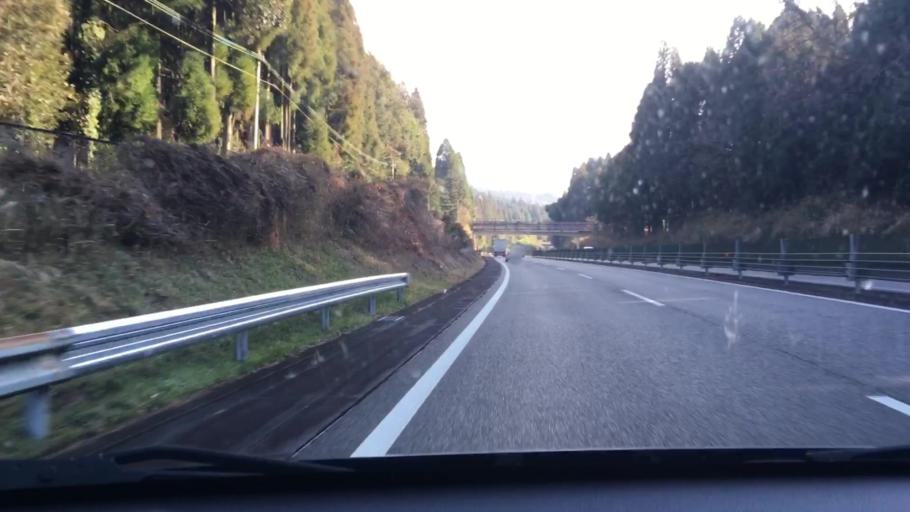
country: JP
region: Kagoshima
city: Okuchi-shinohara
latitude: 32.0031
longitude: 130.7565
